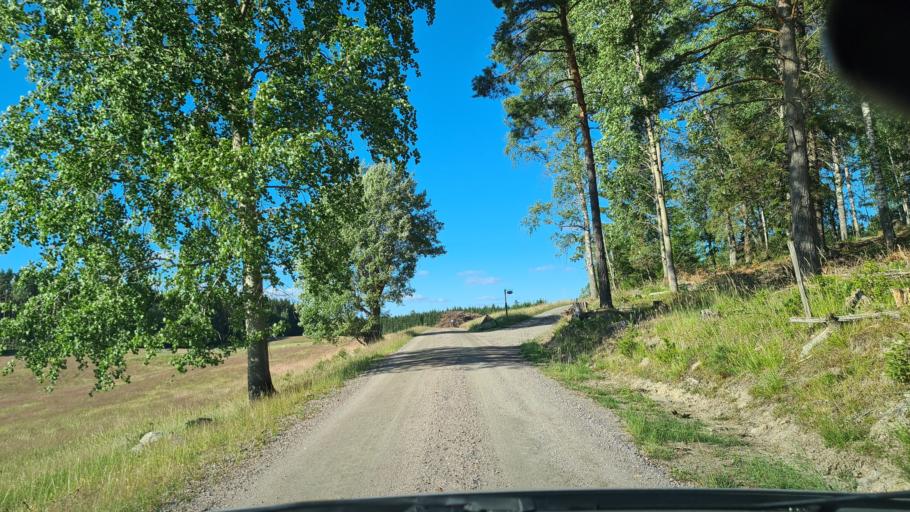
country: SE
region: Soedermanland
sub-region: Nykopings Kommun
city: Stigtomta
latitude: 58.9244
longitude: 16.8904
